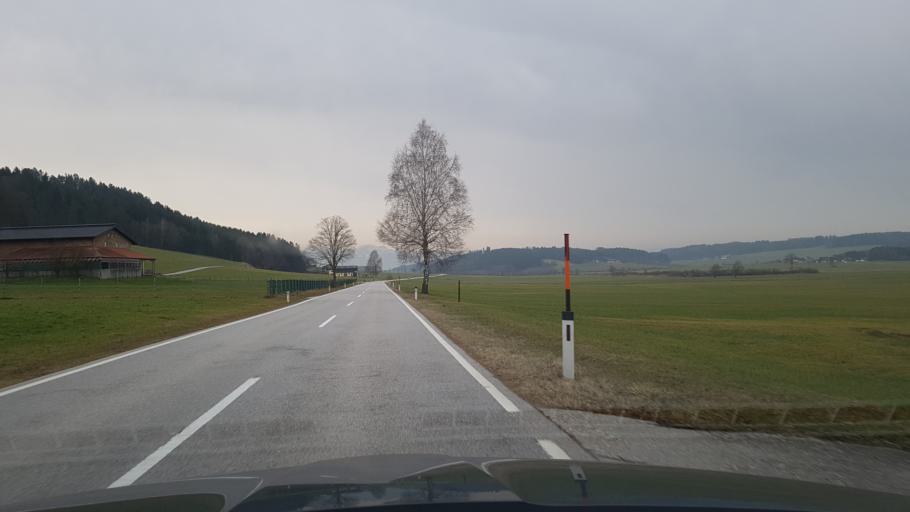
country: AT
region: Salzburg
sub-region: Politischer Bezirk Salzburg-Umgebung
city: Dorfbeuern
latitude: 47.9920
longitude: 13.0208
